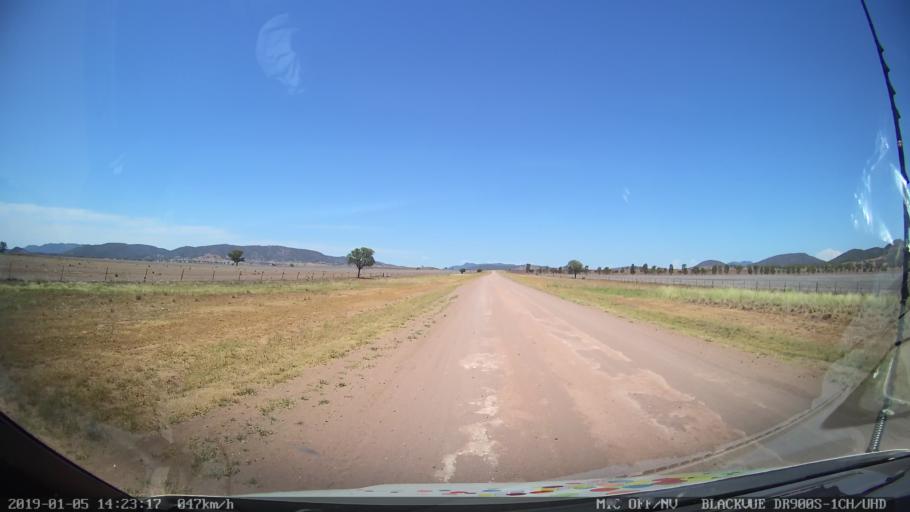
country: AU
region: New South Wales
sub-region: Liverpool Plains
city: Quirindi
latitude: -31.2429
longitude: 150.5286
